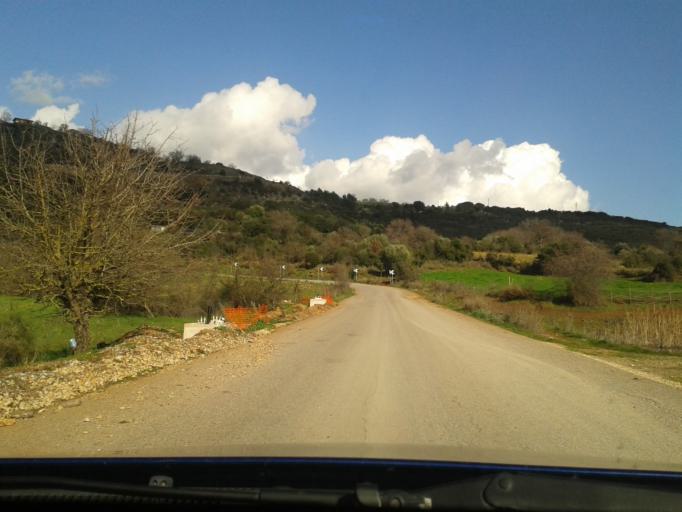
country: GR
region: West Greece
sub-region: Nomos Aitolias kai Akarnanias
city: Fitiai
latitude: 38.6872
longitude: 21.1789
